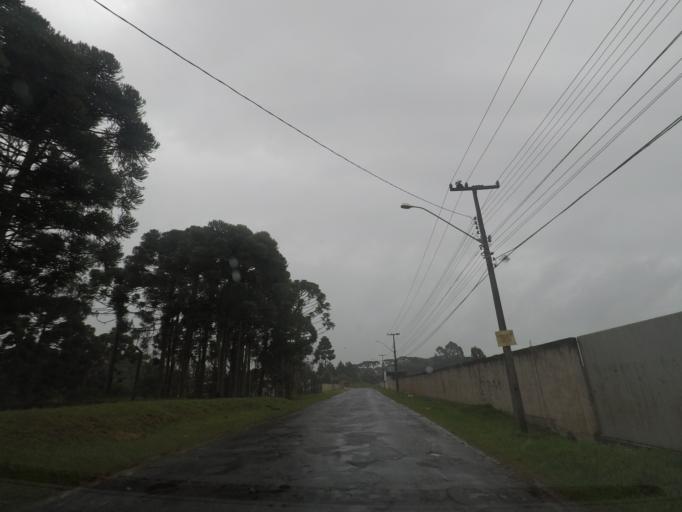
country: BR
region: Parana
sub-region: Campo Largo
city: Campo Largo
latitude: -25.4621
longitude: -49.4166
